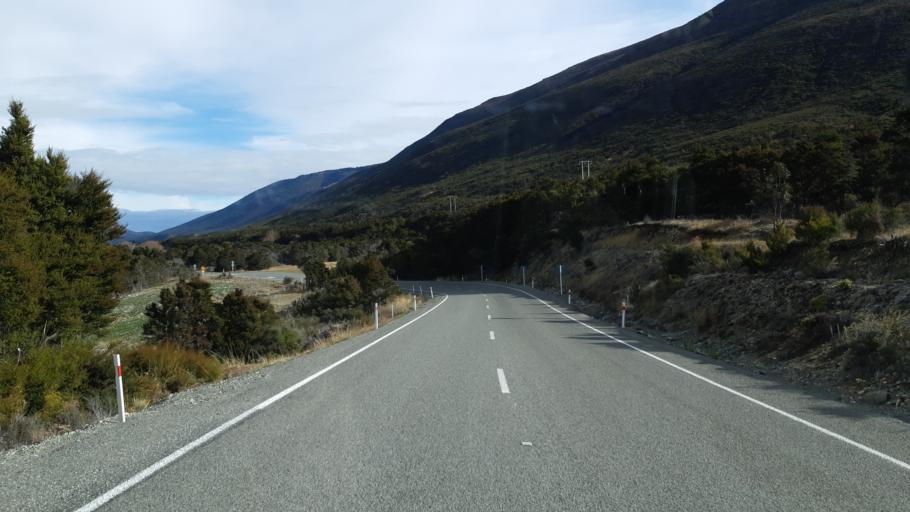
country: NZ
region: Tasman
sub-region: Tasman District
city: Wakefield
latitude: -41.7293
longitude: 173.0378
